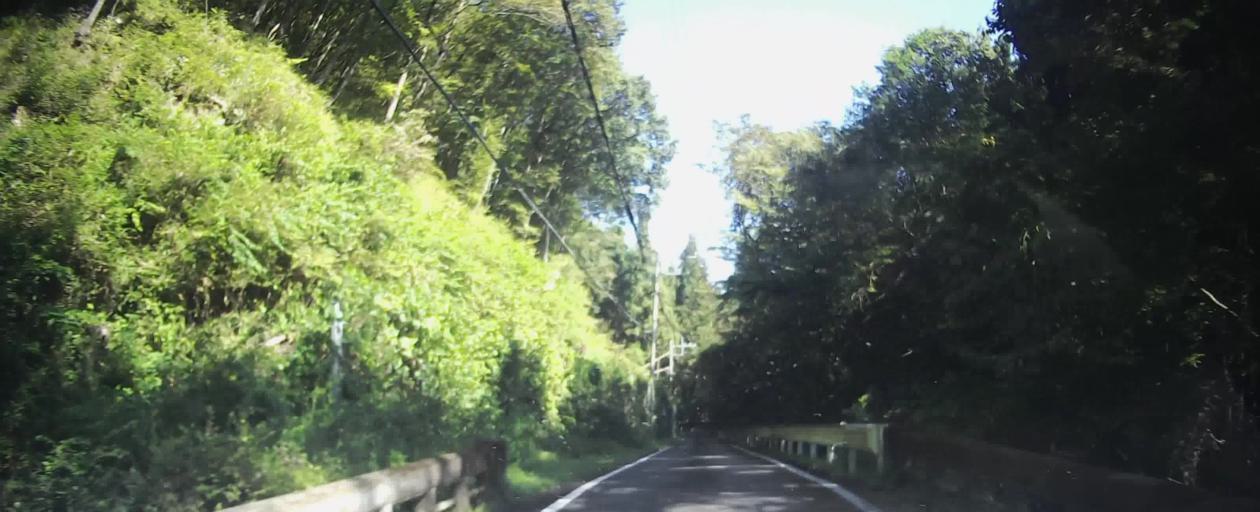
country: JP
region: Gunma
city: Nakanojomachi
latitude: 36.5788
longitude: 138.7276
